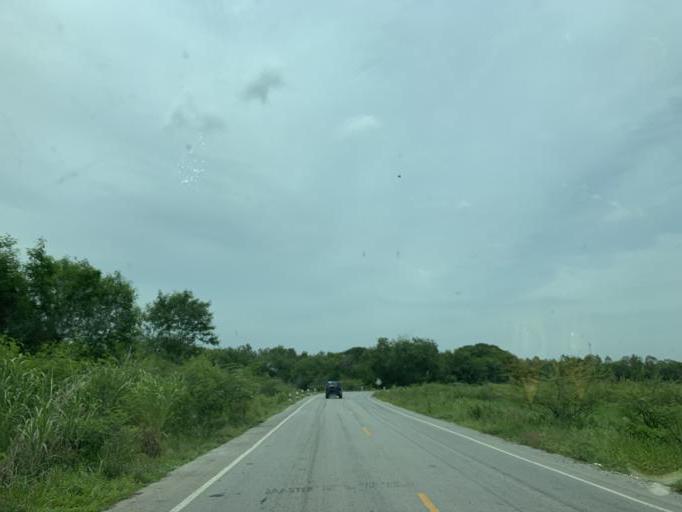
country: TH
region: Uthai Thani
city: Uthai Thani
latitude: 15.4060
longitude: 100.0239
